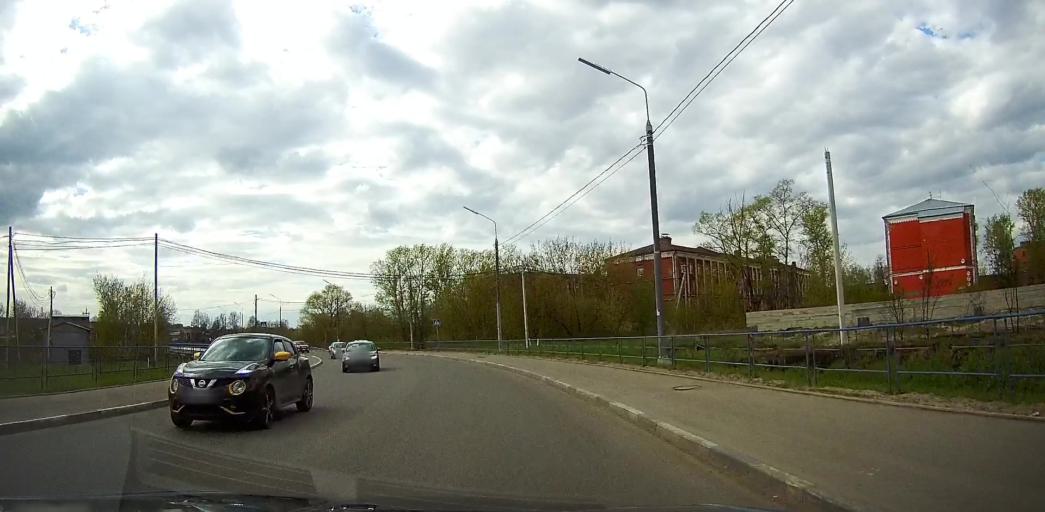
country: RU
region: Moskovskaya
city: Pavlovskiy Posad
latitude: 55.7697
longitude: 38.6489
